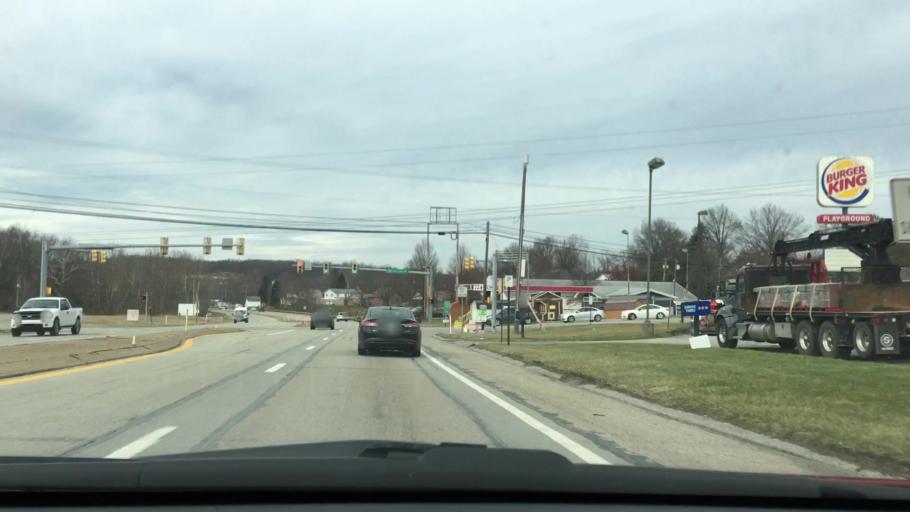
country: US
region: Pennsylvania
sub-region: Westmoreland County
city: Fellsburg
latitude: 40.1581
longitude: -79.7779
